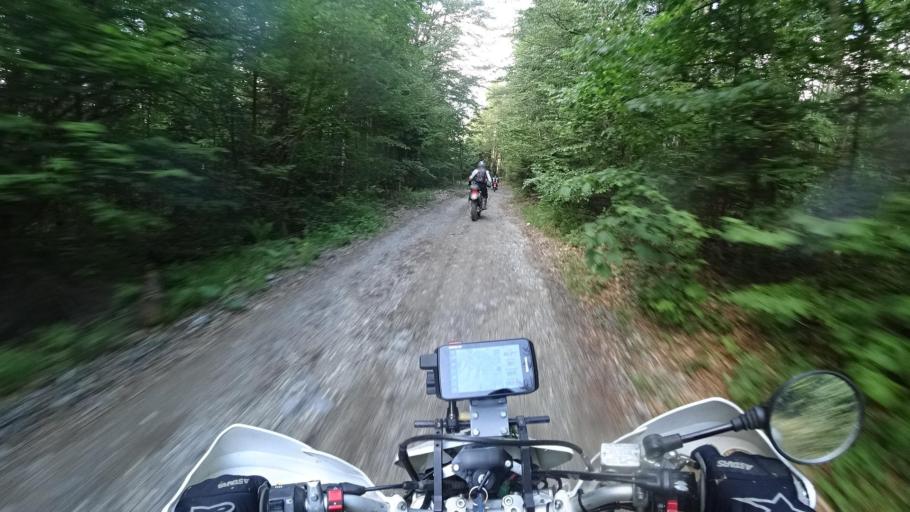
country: BA
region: Federation of Bosnia and Herzegovina
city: Sanica
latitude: 44.6730
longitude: 16.5092
